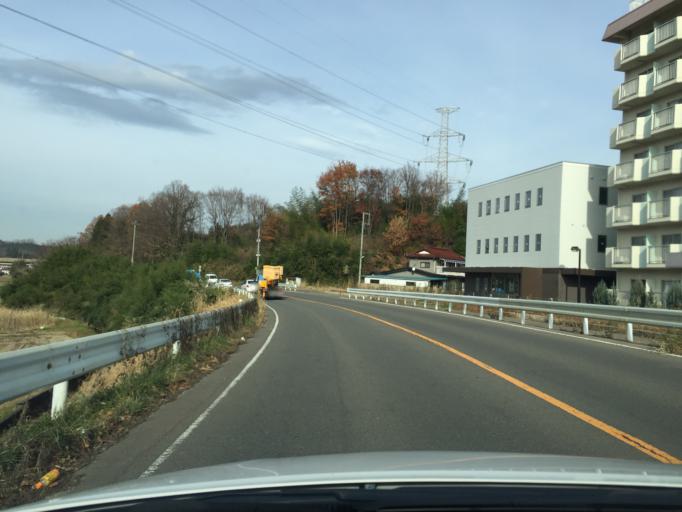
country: JP
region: Fukushima
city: Fukushima-shi
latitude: 37.6723
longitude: 140.4663
